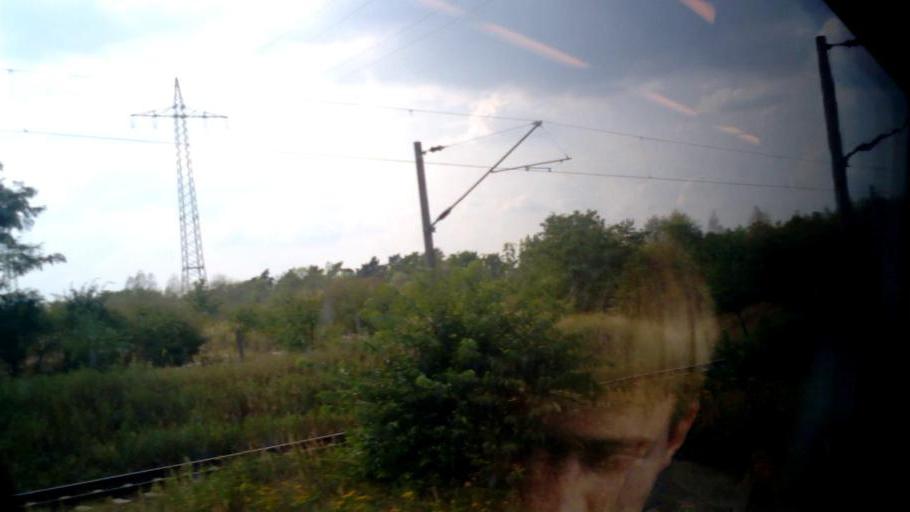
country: DE
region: Brandenburg
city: Ludwigsfelde
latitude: 52.3332
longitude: 13.2580
